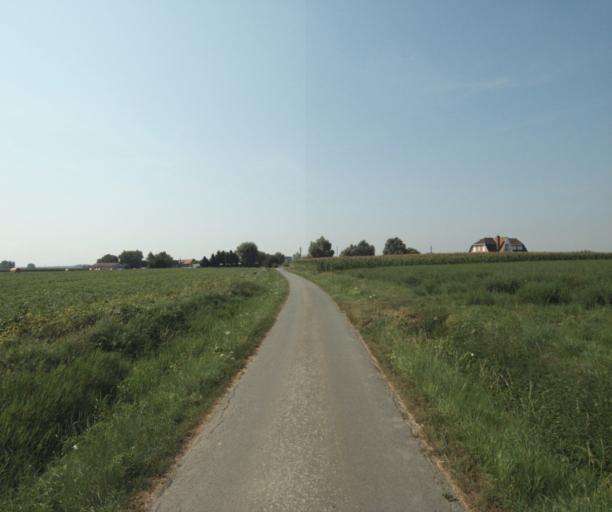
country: FR
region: Nord-Pas-de-Calais
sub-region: Departement du Nord
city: Quesnoy-sur-Deule
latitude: 50.7107
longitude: 2.9815
